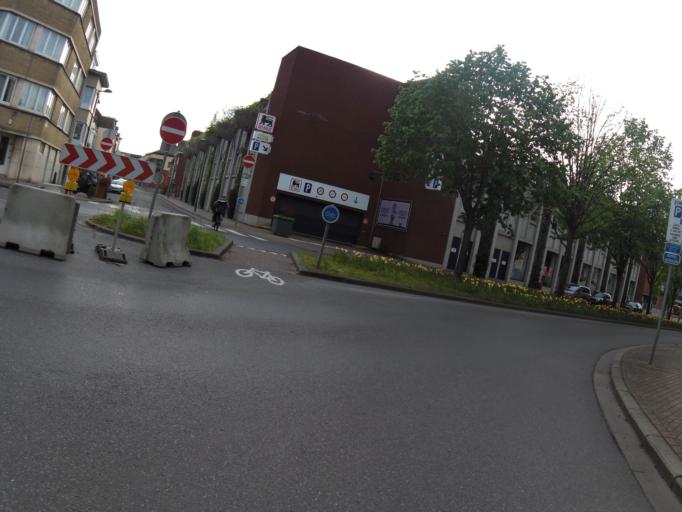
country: BE
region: Flanders
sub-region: Provincie Vlaams-Brabant
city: Kraainem
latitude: 50.8478
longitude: 4.4298
